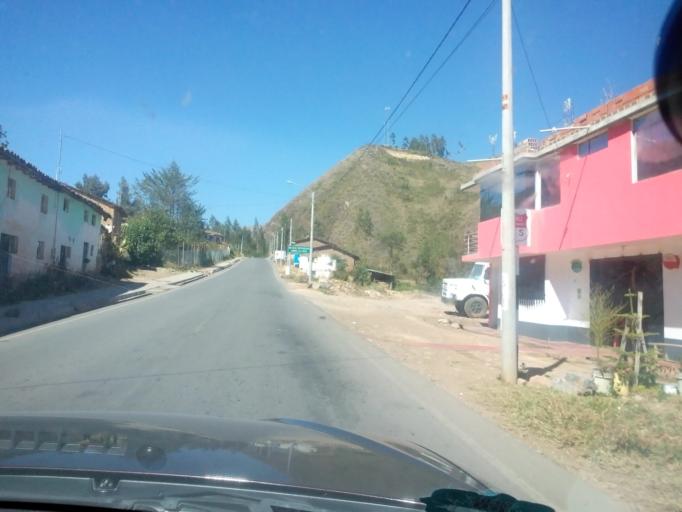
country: PE
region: Apurimac
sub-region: Chincheros
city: Chincheros
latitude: -13.5142
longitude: -73.7107
